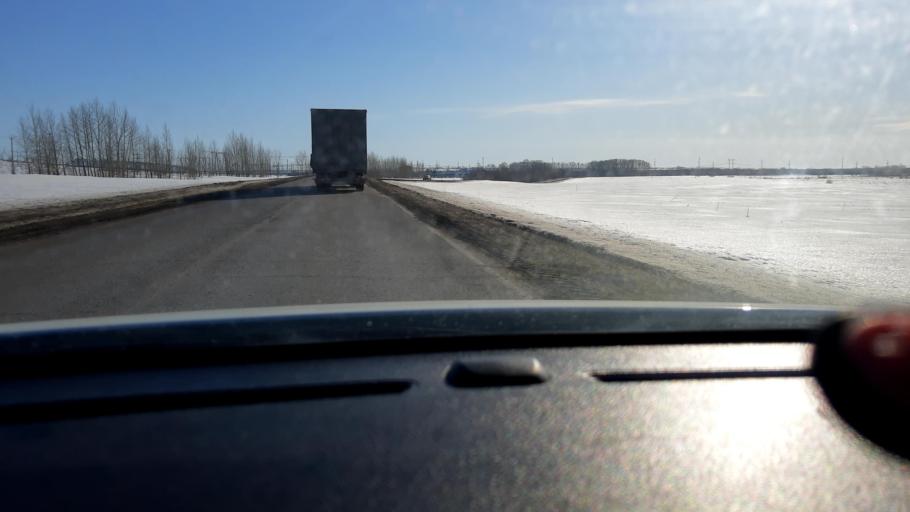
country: RU
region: Bashkortostan
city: Avdon
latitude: 54.4410
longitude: 55.8384
